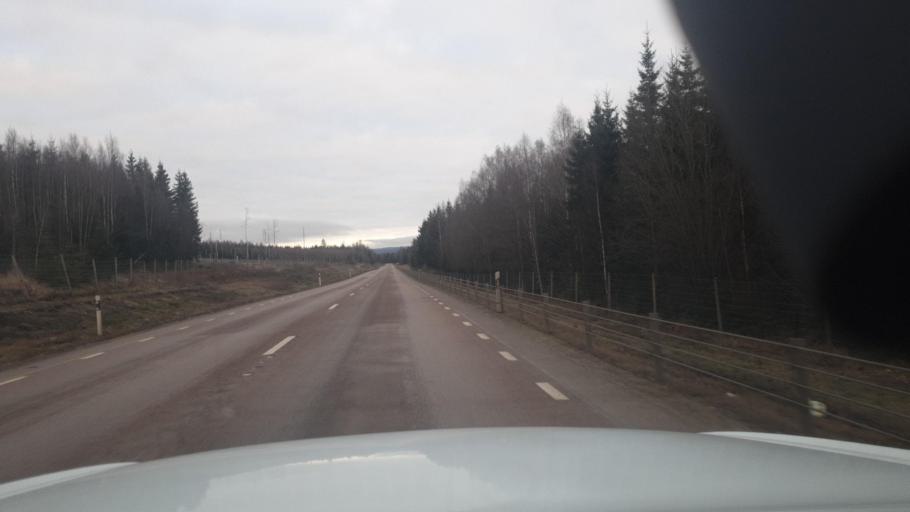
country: SE
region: Vaermland
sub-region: Sunne Kommun
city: Sunne
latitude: 59.7537
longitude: 13.1184
